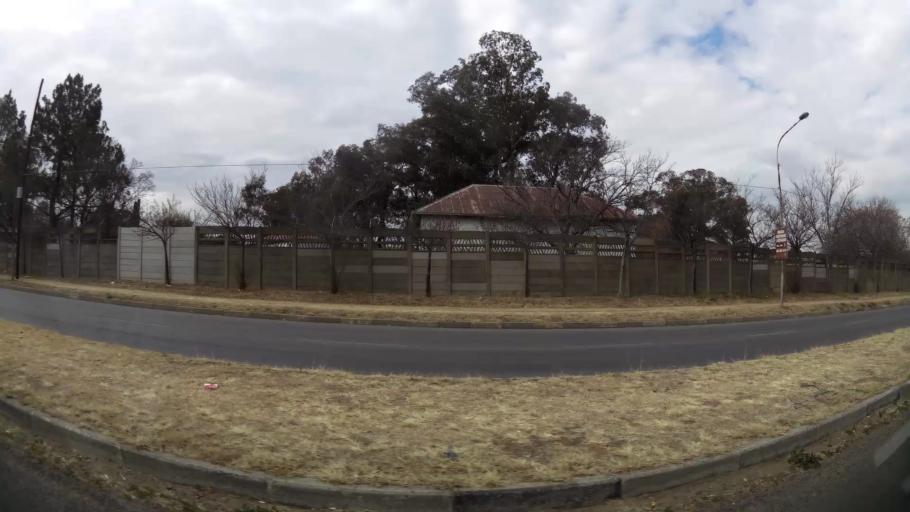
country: ZA
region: Orange Free State
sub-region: Fezile Dabi District Municipality
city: Kroonstad
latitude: -27.6543
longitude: 27.2308
